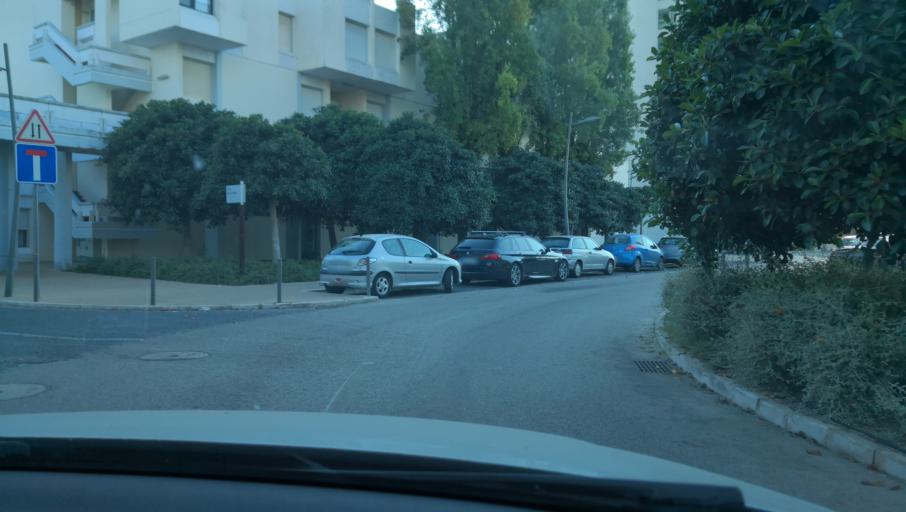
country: PT
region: Setubal
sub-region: Setubal
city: Setubal
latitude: 38.4920
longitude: -8.9036
